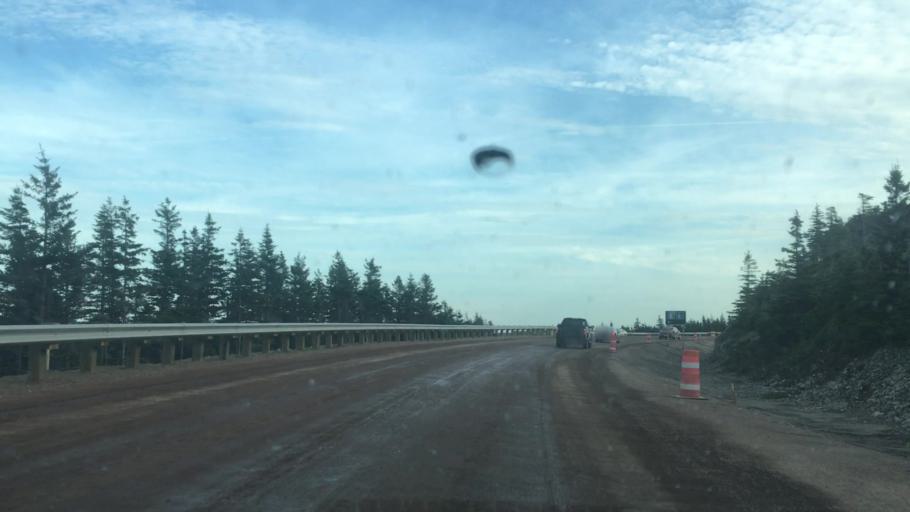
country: CA
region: Nova Scotia
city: Sydney Mines
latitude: 46.8046
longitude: -60.8438
